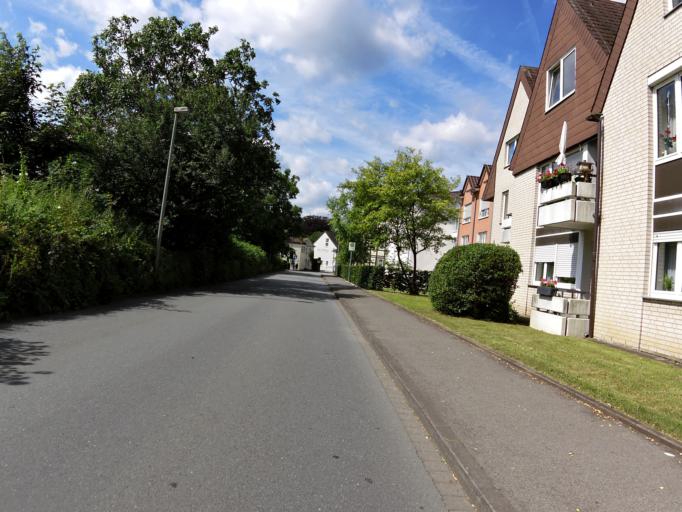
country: DE
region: North Rhine-Westphalia
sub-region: Regierungsbezirk Detmold
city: Hoexter
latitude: 51.7752
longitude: 9.3865
